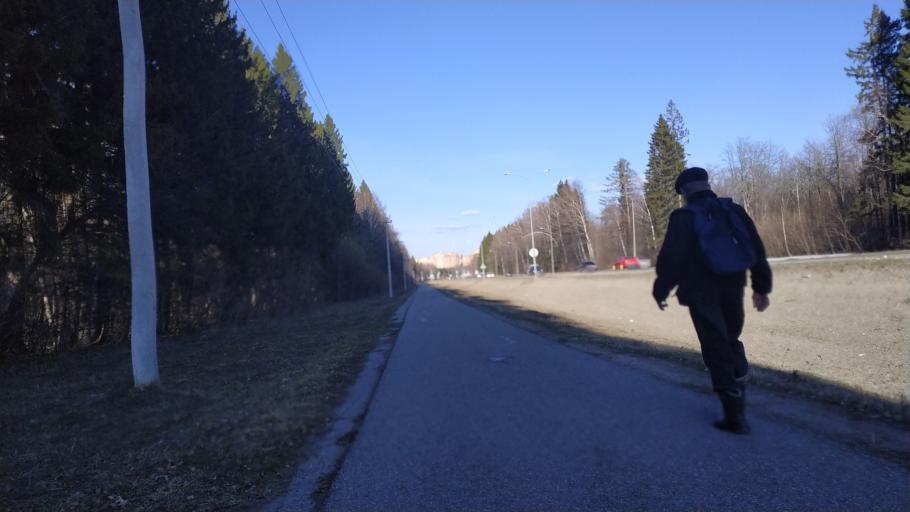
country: RU
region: Chuvashia
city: Novyye Lapsary
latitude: 56.1285
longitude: 47.1293
